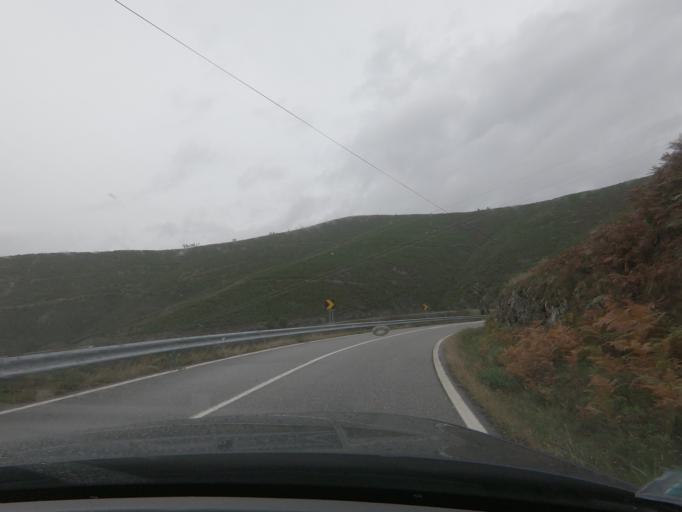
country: PT
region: Vila Real
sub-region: Mondim de Basto
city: Mondim de Basto
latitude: 41.3574
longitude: -7.9172
